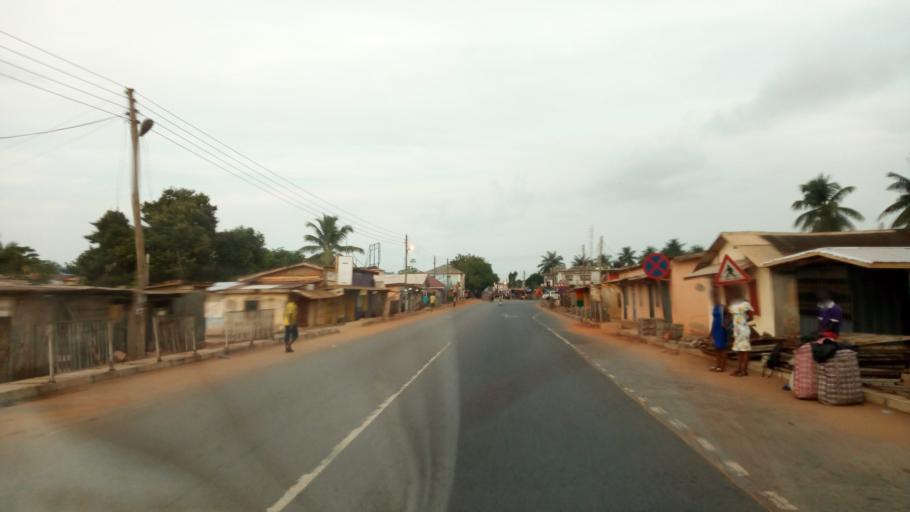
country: TG
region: Maritime
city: Lome
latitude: 6.1021
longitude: 1.1485
